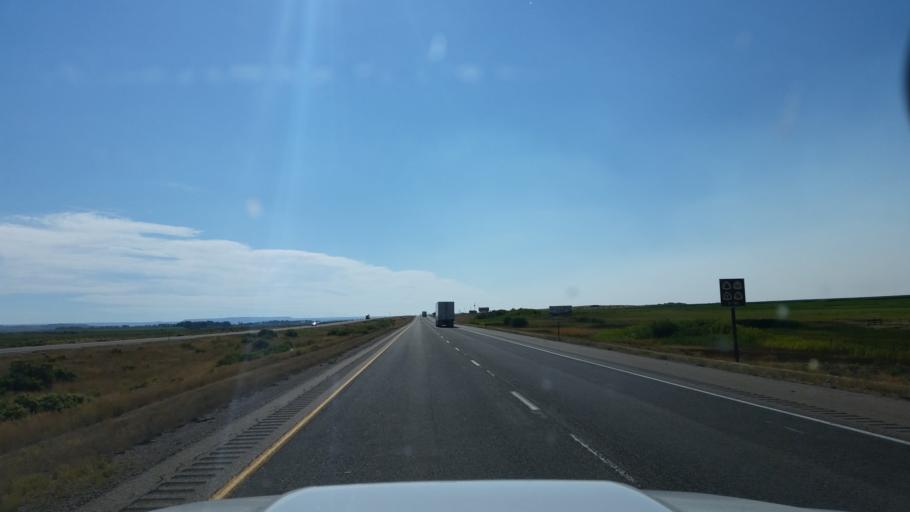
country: US
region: Wyoming
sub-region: Uinta County
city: Lyman
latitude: 41.3740
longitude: -110.2489
